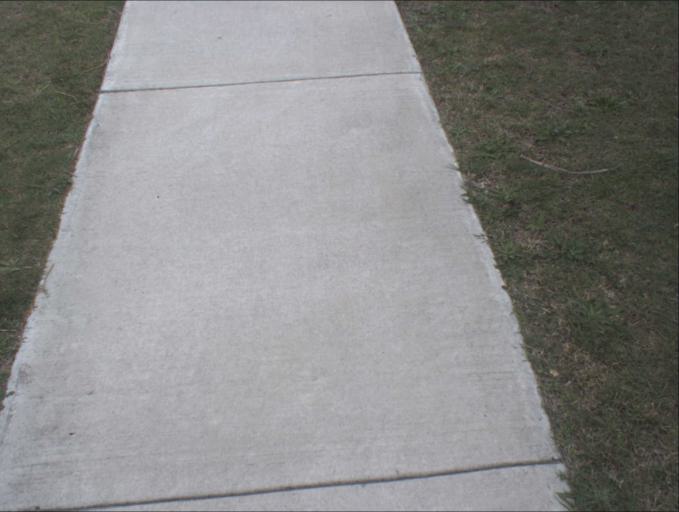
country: AU
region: Queensland
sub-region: Logan
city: Park Ridge South
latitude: -27.6696
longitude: 153.0388
